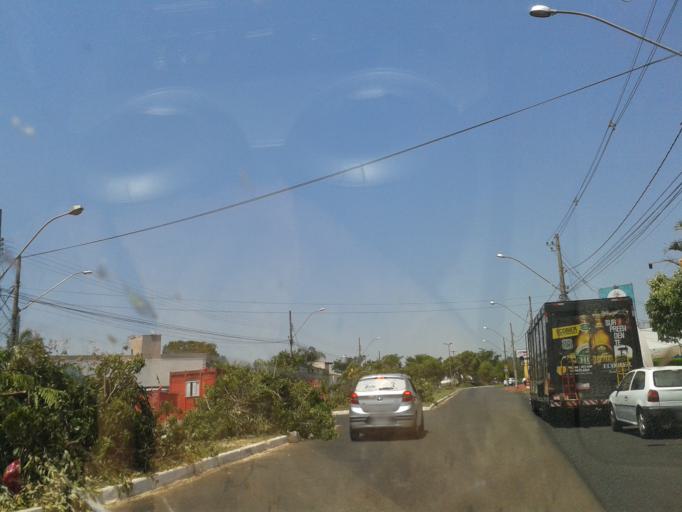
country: BR
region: Minas Gerais
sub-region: Uberlandia
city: Uberlandia
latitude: -18.9374
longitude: -48.3064
